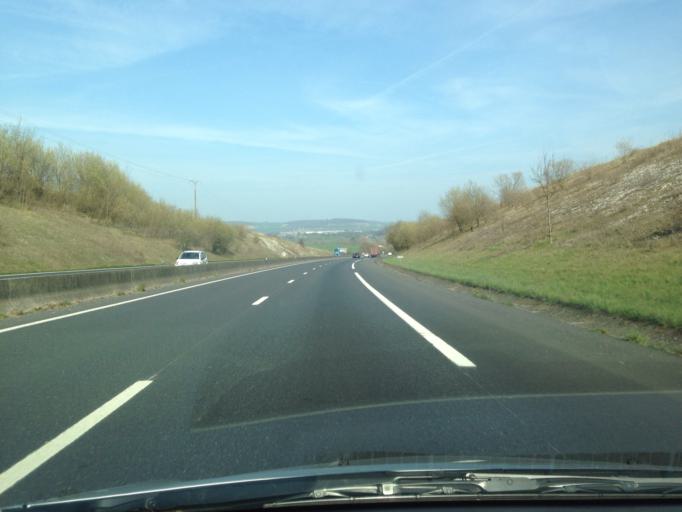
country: FR
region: Haute-Normandie
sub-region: Departement de la Seine-Maritime
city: Mesnieres-en-Bray
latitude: 49.7113
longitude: 1.3841
